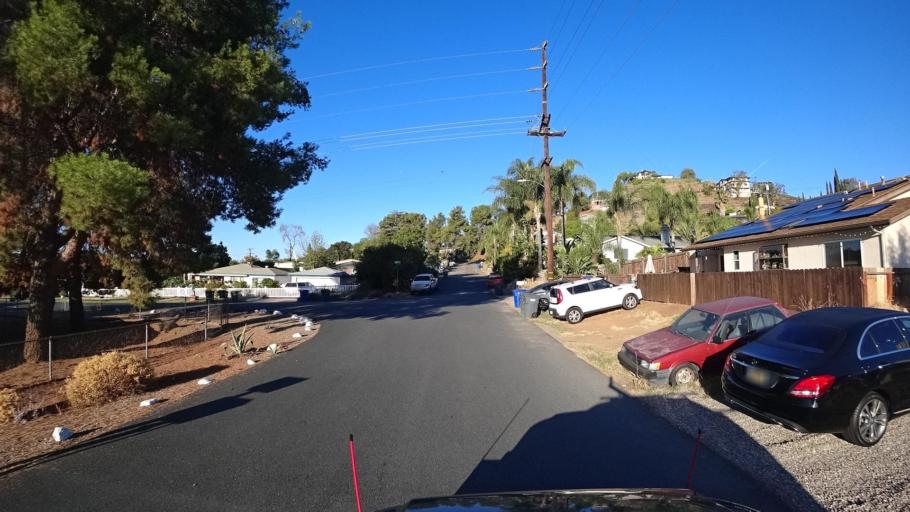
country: US
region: California
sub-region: San Diego County
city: Bostonia
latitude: 32.8154
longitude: -116.9399
